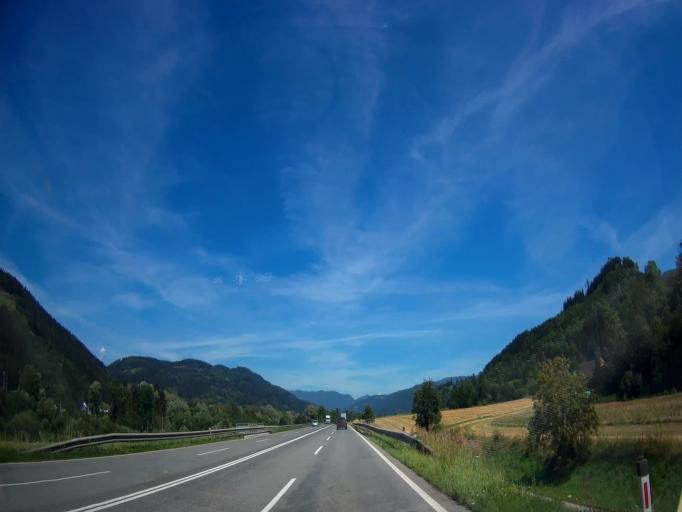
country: AT
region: Carinthia
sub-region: Politischer Bezirk Sankt Veit an der Glan
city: Micheldorf
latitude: 46.9052
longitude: 14.4388
